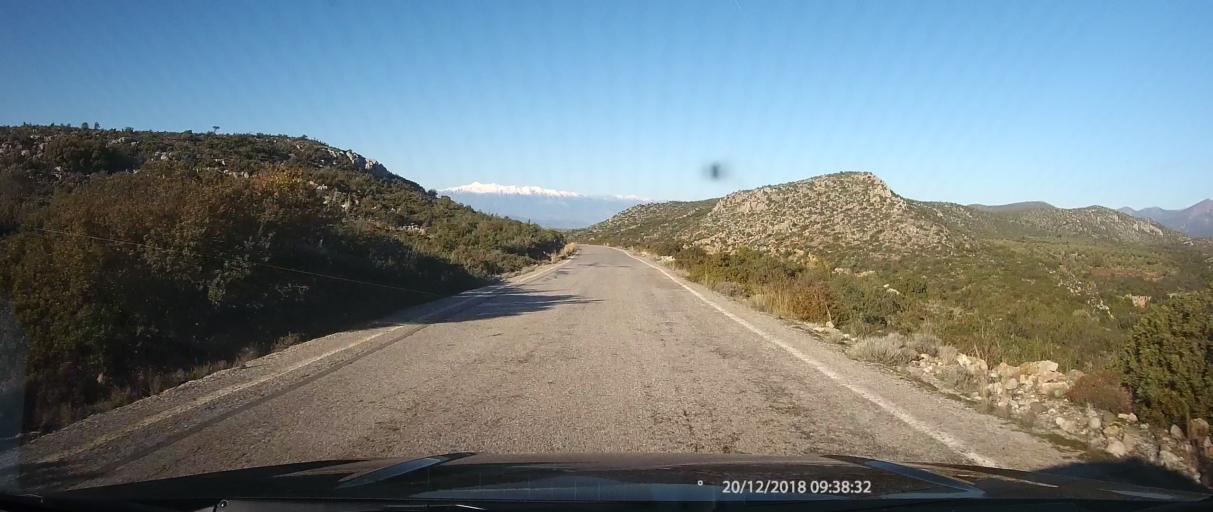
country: GR
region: Peloponnese
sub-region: Nomos Lakonias
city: Kato Glikovrisi
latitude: 36.9394
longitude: 22.7897
